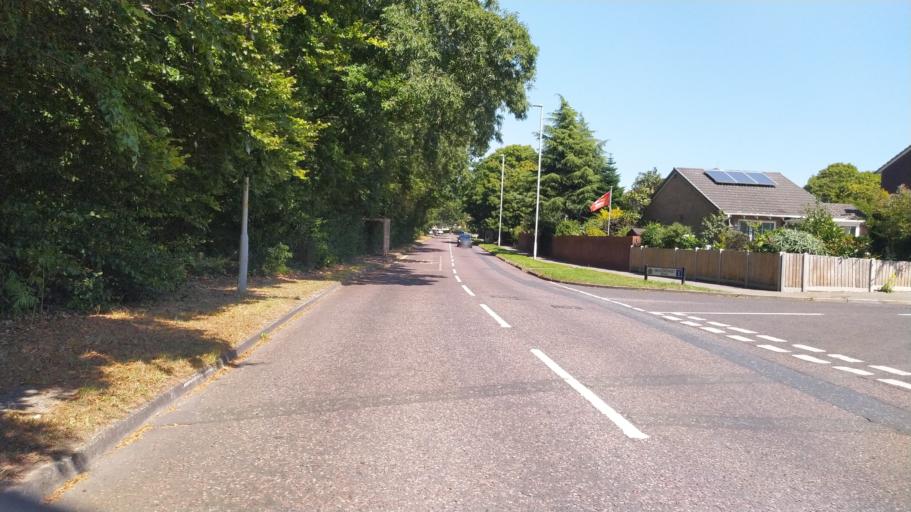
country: GB
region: England
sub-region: Dorset
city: Broadstone
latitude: 50.7450
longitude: -2.0119
